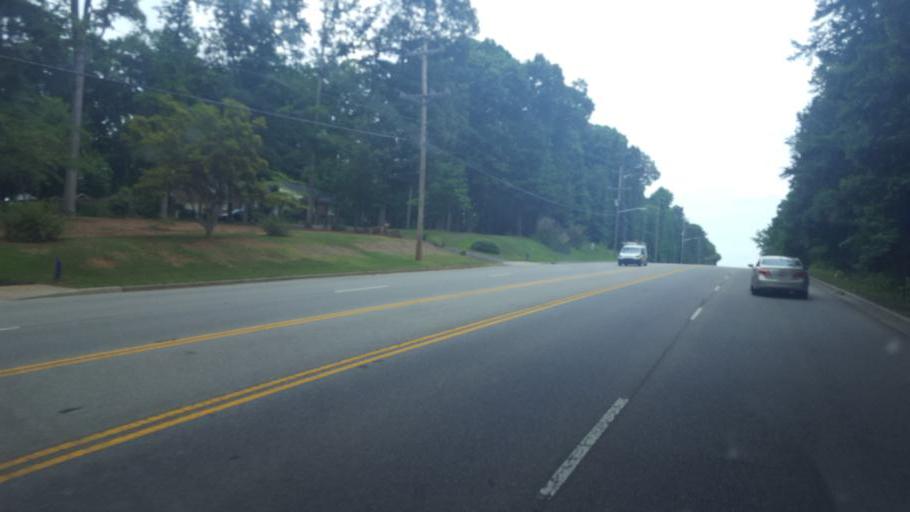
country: US
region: South Carolina
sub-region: York County
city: Newport
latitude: 34.9547
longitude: -81.0919
